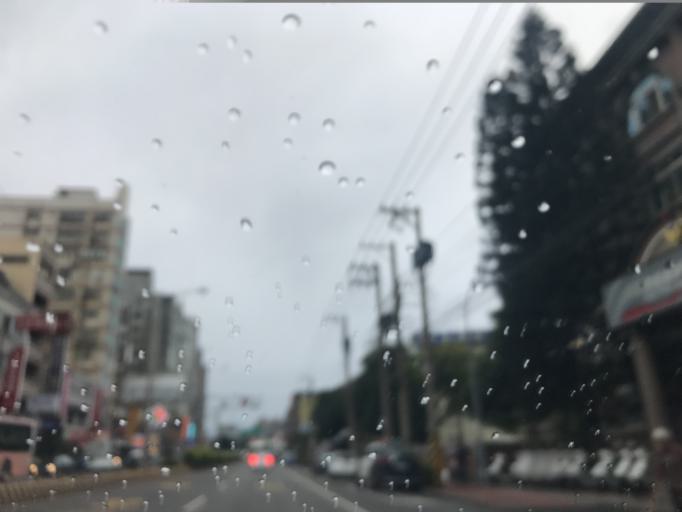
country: TW
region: Taiwan
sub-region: Hsinchu
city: Zhubei
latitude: 24.8387
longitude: 121.0052
